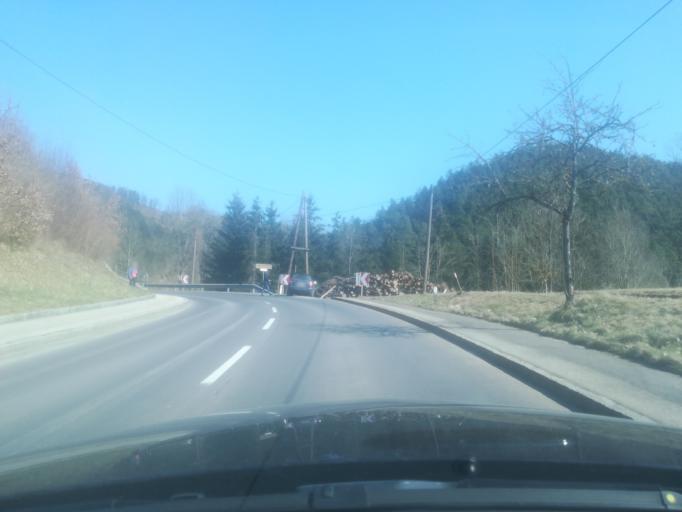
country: AT
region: Upper Austria
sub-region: Politischer Bezirk Freistadt
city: Freistadt
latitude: 48.4421
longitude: 14.5421
